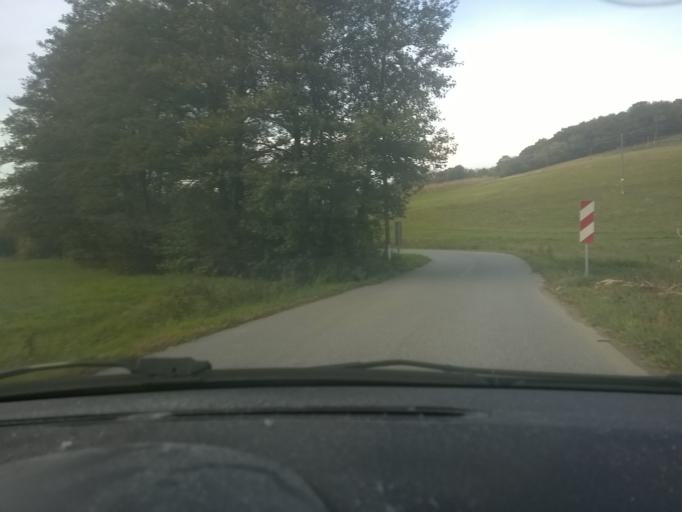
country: HR
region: Krapinsko-Zagorska
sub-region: Grad Krapina
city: Krapina
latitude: 46.1234
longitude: 15.8516
